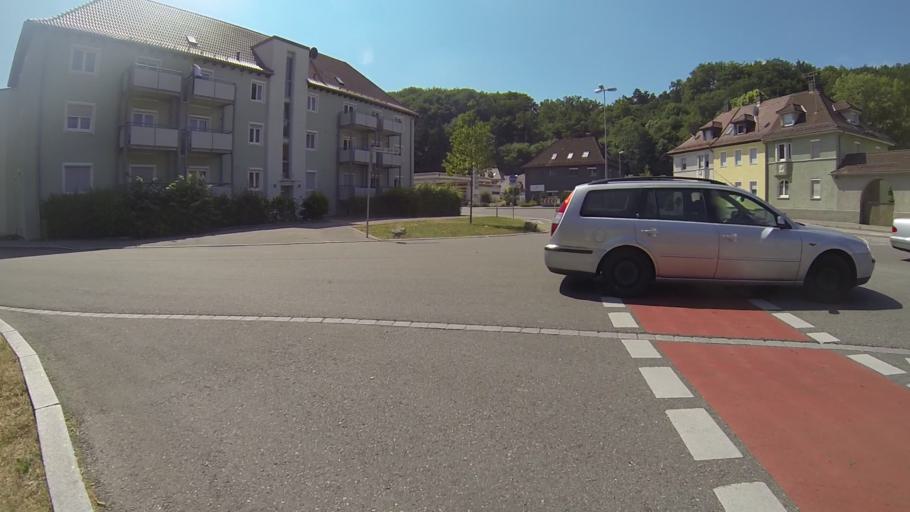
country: DE
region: Baden-Wuerttemberg
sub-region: Regierungsbezirk Stuttgart
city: Heidenheim an der Brenz
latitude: 48.6676
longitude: 10.1619
